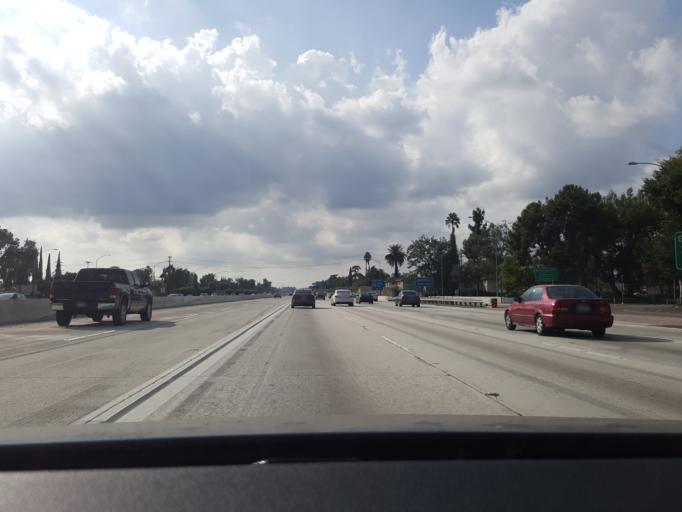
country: US
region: California
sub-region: Los Angeles County
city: Monterey Park
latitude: 34.0718
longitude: -118.1217
